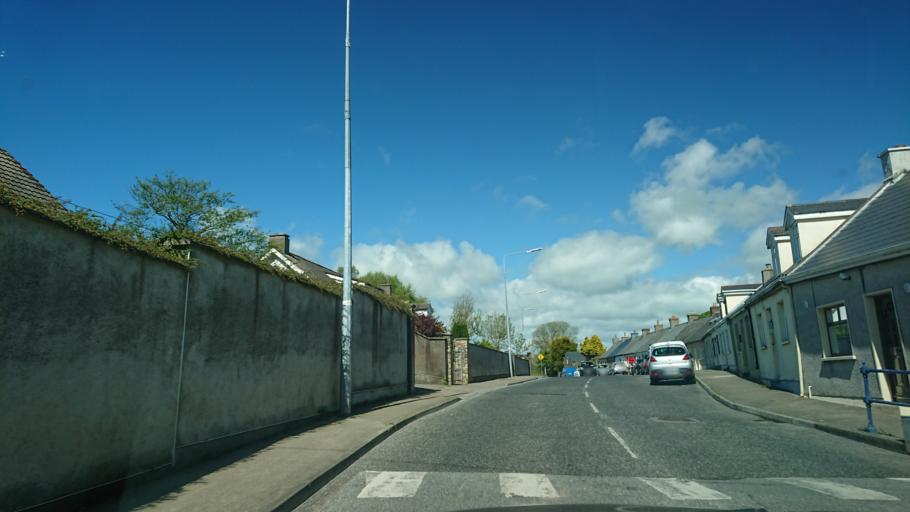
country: IE
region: Munster
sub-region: Waterford
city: Waterford
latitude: 52.2639
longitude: -7.1306
